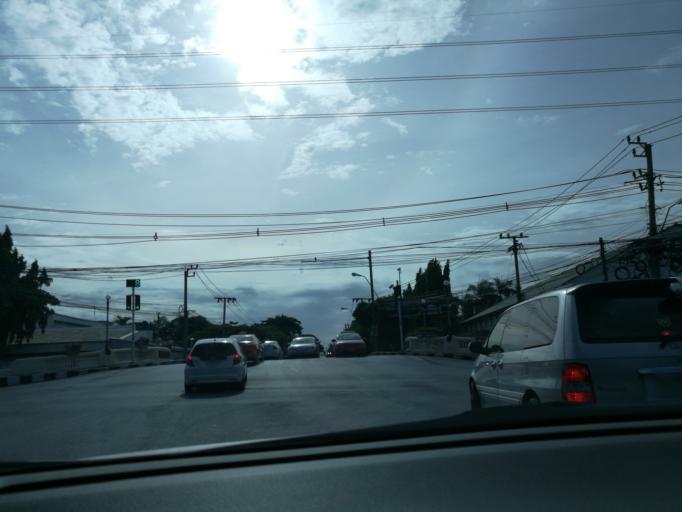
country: TH
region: Bangkok
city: Bang Sue
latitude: 13.7934
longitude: 100.5301
